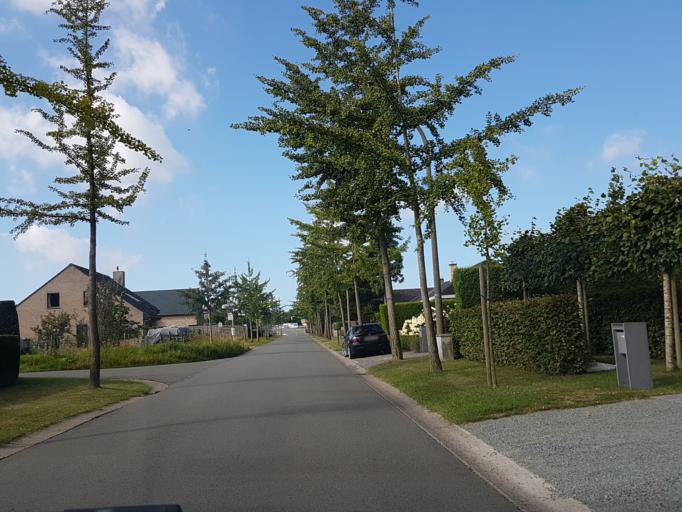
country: BE
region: Flanders
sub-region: Provincie Oost-Vlaanderen
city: Aalter
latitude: 51.0919
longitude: 3.4602
